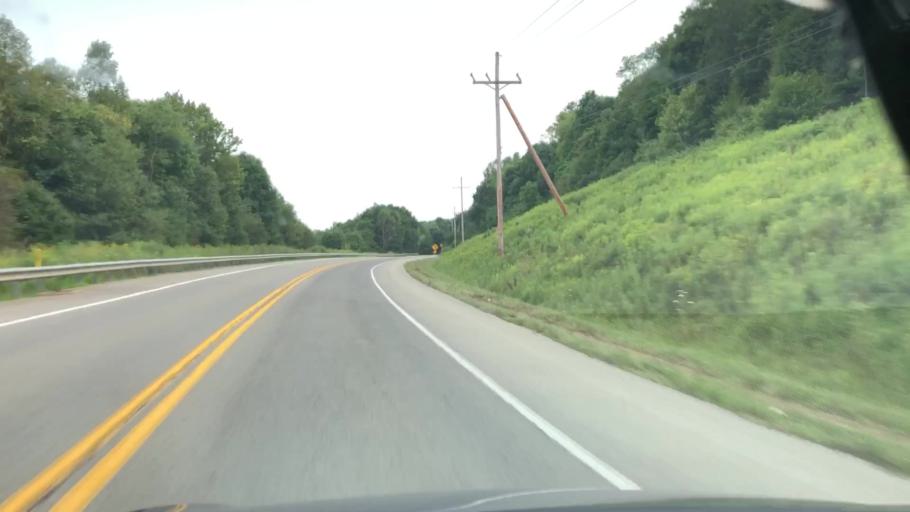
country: US
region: Pennsylvania
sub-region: Venango County
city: Hasson Heights
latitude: 41.5246
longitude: -79.7106
